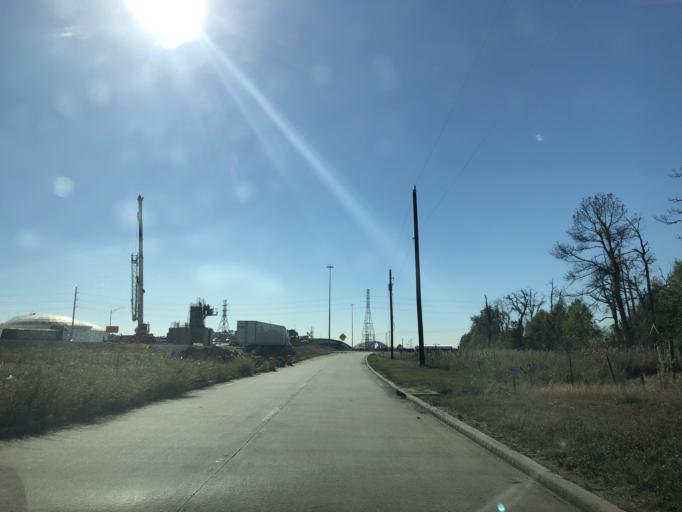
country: US
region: Texas
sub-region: Harris County
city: Cloverleaf
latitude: 29.7591
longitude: -95.1467
